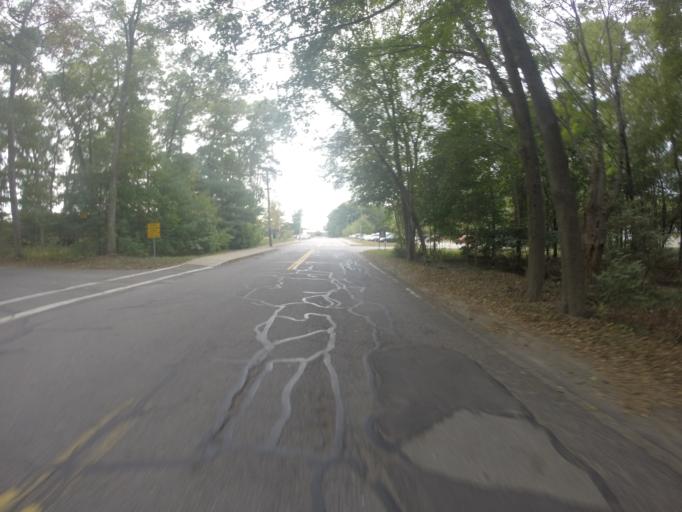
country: US
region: Massachusetts
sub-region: Bristol County
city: Easton
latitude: 42.0588
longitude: -71.1070
